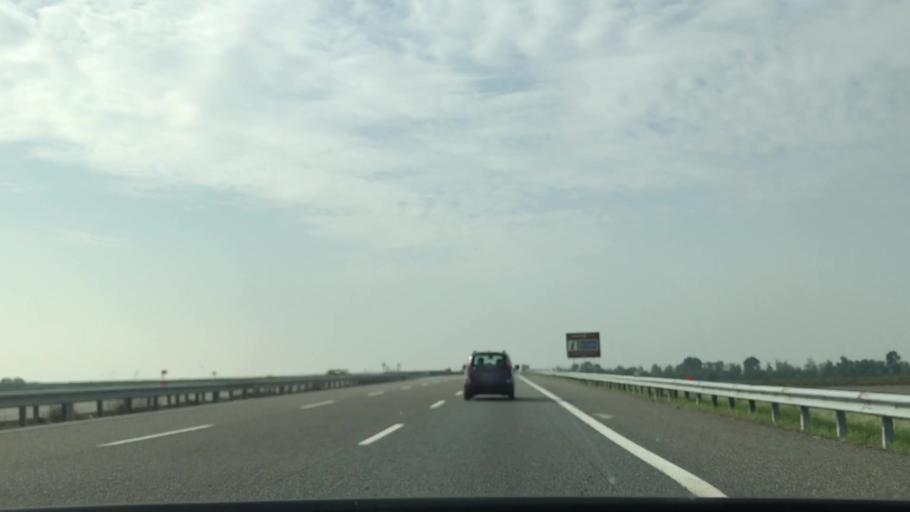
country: IT
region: Piedmont
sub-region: Provincia di Vercelli
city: Prarolo
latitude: 45.3169
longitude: 8.4701
